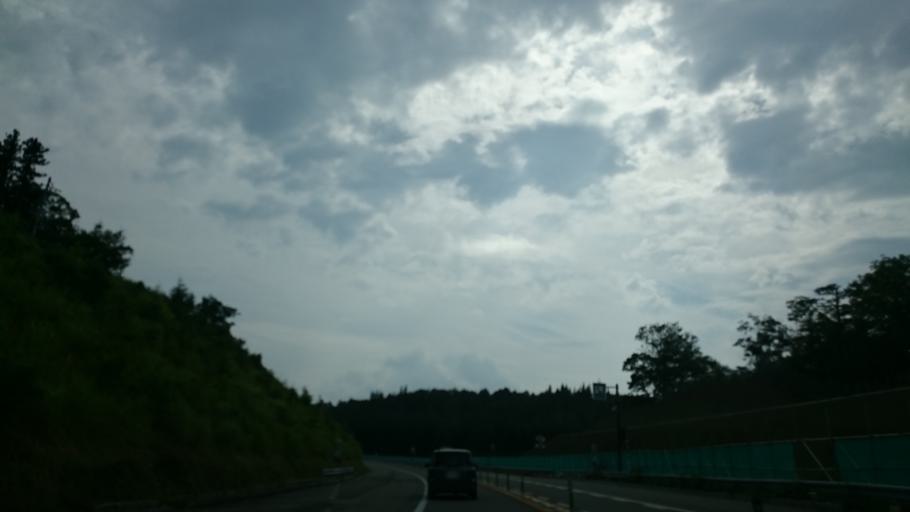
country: JP
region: Gifu
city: Gujo
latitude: 36.0171
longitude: 136.9344
